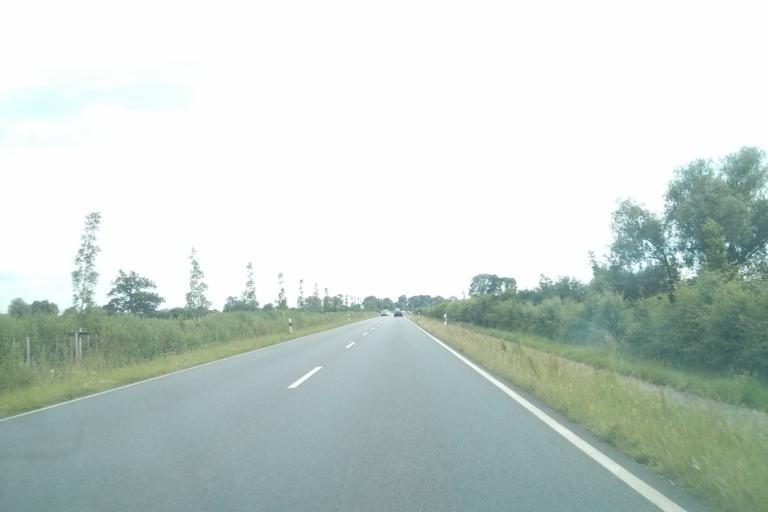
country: DE
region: Lower Saxony
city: Achim
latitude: 52.9907
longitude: 9.0533
